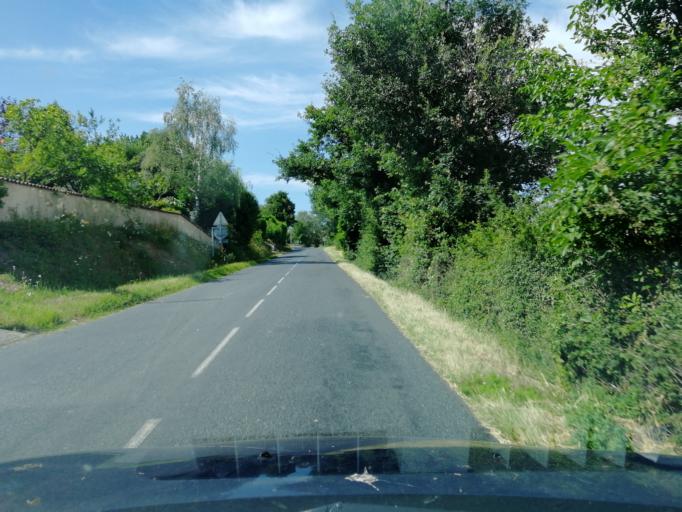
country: FR
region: Rhone-Alpes
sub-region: Departement du Rhone
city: Mornant
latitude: 45.6323
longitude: 4.6435
